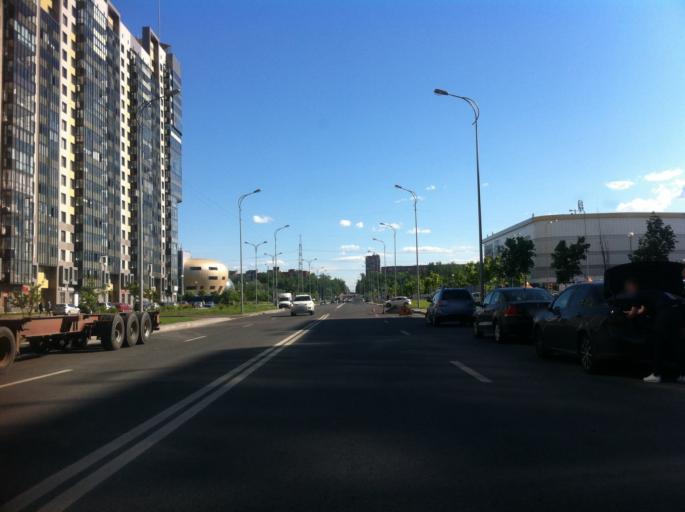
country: RU
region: St.-Petersburg
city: Sosnovaya Polyana
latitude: 59.8515
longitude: 30.1470
